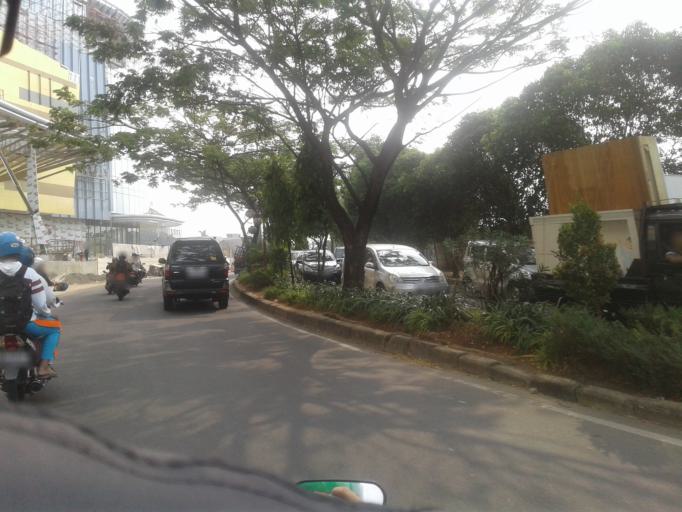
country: ID
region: West Java
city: Depok
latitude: -6.3798
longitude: 106.8447
